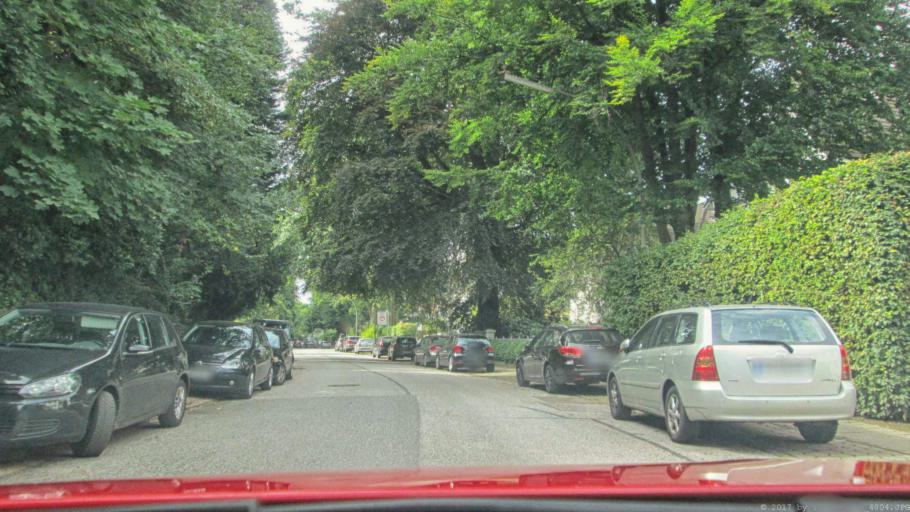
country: DE
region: Schleswig-Holstein
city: Halstenbek
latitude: 53.5603
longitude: 9.8176
